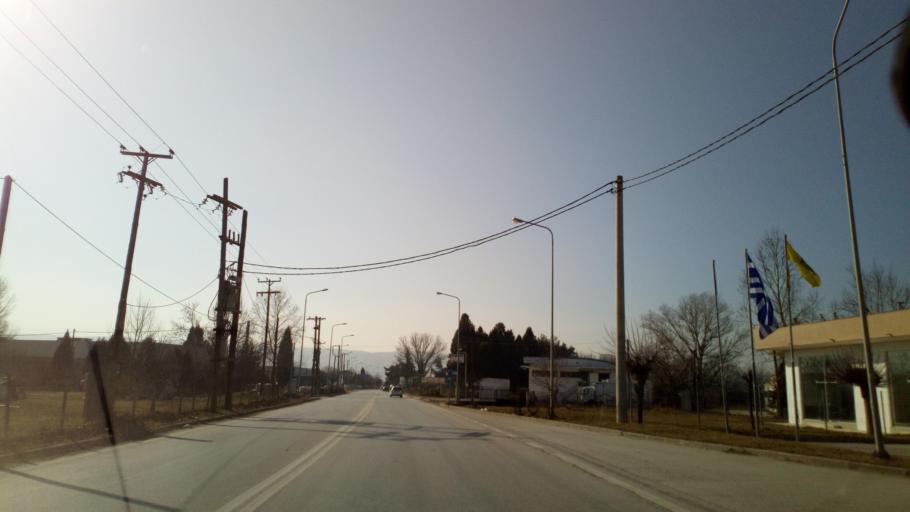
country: GR
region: Central Macedonia
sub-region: Nomos Thessalonikis
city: Lagkadas
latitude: 40.7419
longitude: 23.0513
